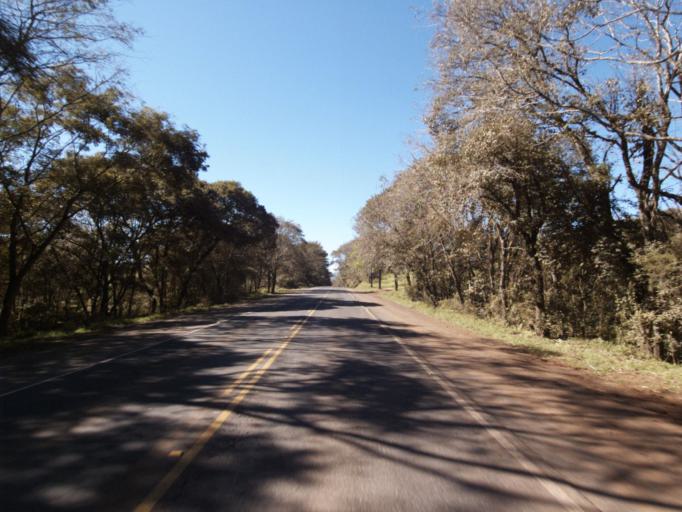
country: BR
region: Santa Catarina
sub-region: Sao Lourenco Do Oeste
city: Sao Lourenco dOeste
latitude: -26.8259
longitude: -53.0633
